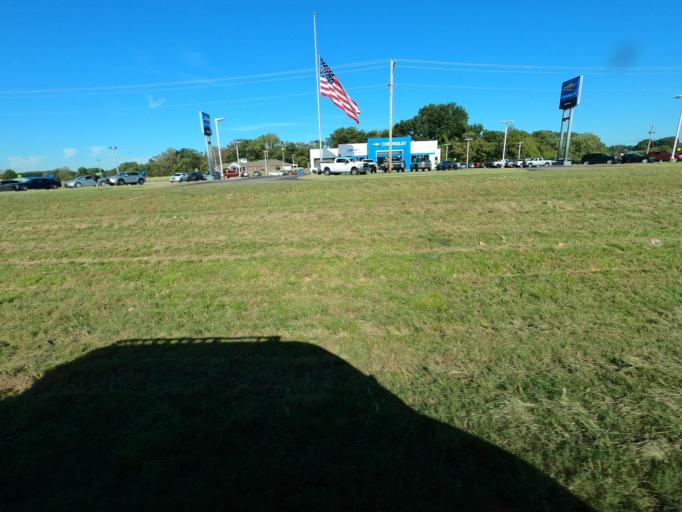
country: US
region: Tennessee
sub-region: Tipton County
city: Covington
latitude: 35.5273
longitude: -89.6870
